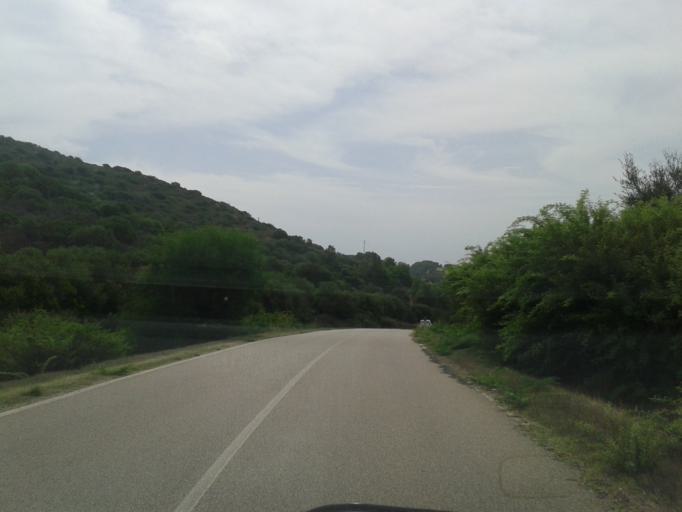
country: IT
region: Sardinia
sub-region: Provincia di Cagliari
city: Villasimius
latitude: 39.1412
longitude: 9.5307
